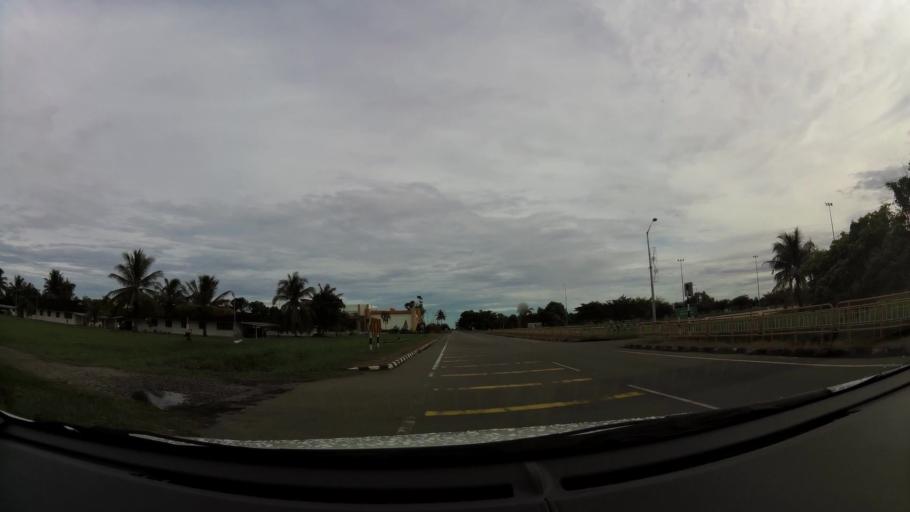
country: BN
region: Belait
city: Seria
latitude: 4.6133
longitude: 114.3265
